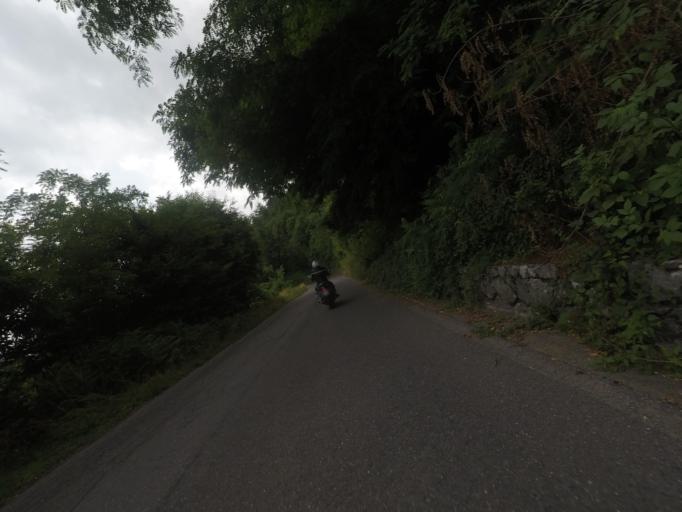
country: IT
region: Tuscany
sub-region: Provincia di Lucca
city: Careggine
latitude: 44.1144
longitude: 10.3625
